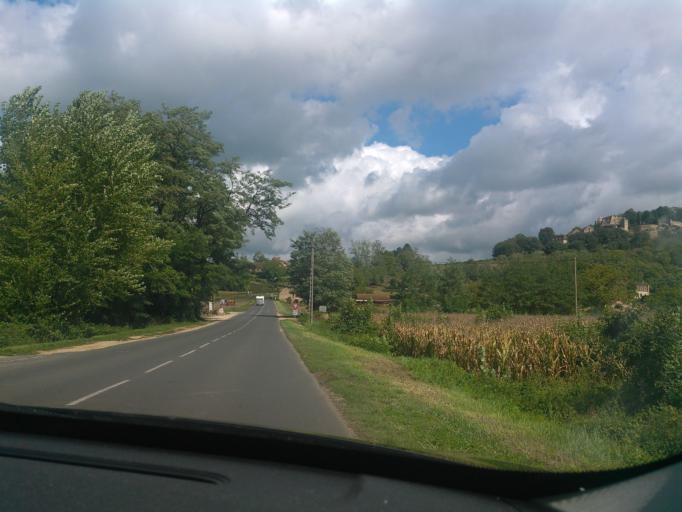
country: FR
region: Aquitaine
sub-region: Departement de la Dordogne
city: Cenac-et-Saint-Julien
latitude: 44.8202
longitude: 1.1561
